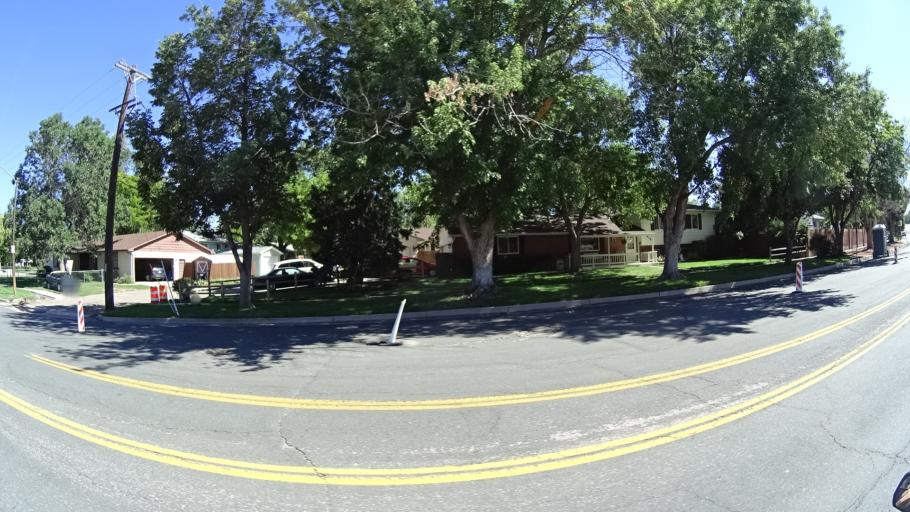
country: US
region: Colorado
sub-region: El Paso County
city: Colorado Springs
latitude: 38.8679
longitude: -104.8048
